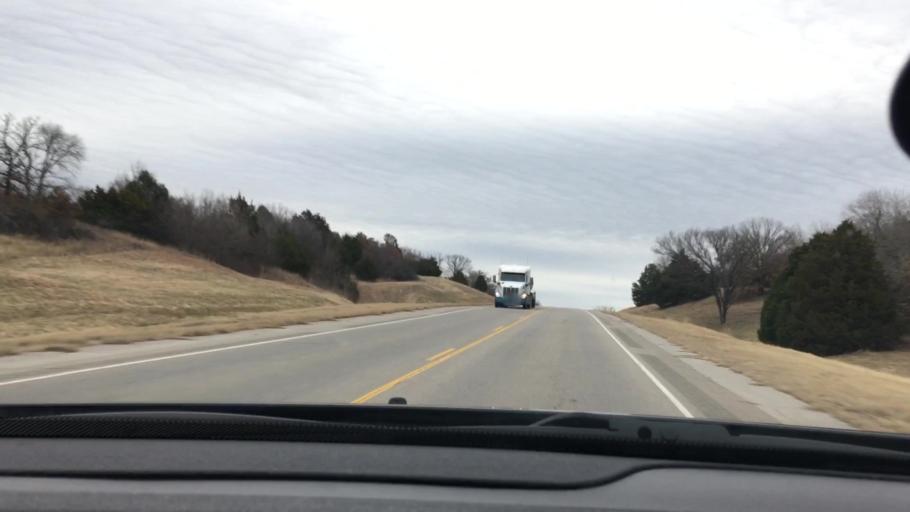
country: US
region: Oklahoma
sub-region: Johnston County
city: Tishomingo
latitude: 34.2363
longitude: -96.7784
